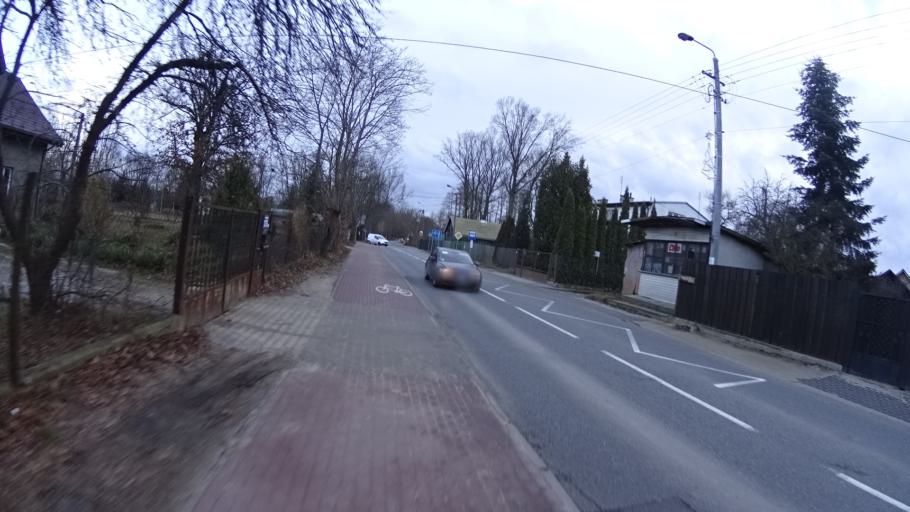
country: PL
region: Masovian Voivodeship
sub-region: Powiat pruszkowski
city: Granica
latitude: 52.1163
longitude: 20.7971
